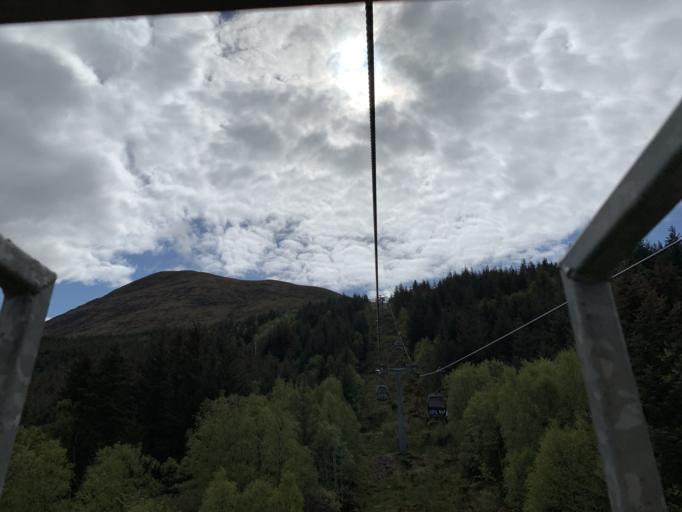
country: GB
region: Scotland
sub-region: Highland
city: Spean Bridge
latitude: 56.8463
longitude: -4.9888
